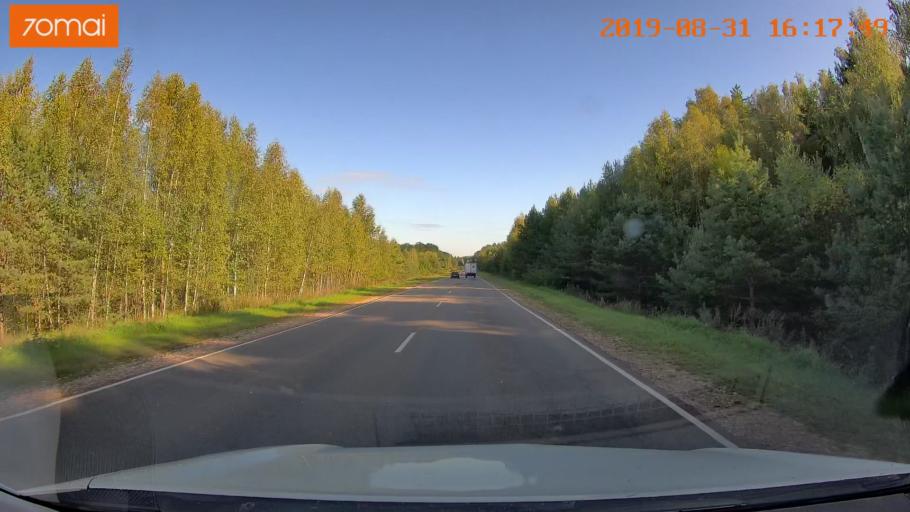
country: RU
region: Kaluga
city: Nikola-Lenivets
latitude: 54.5422
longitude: 35.5419
